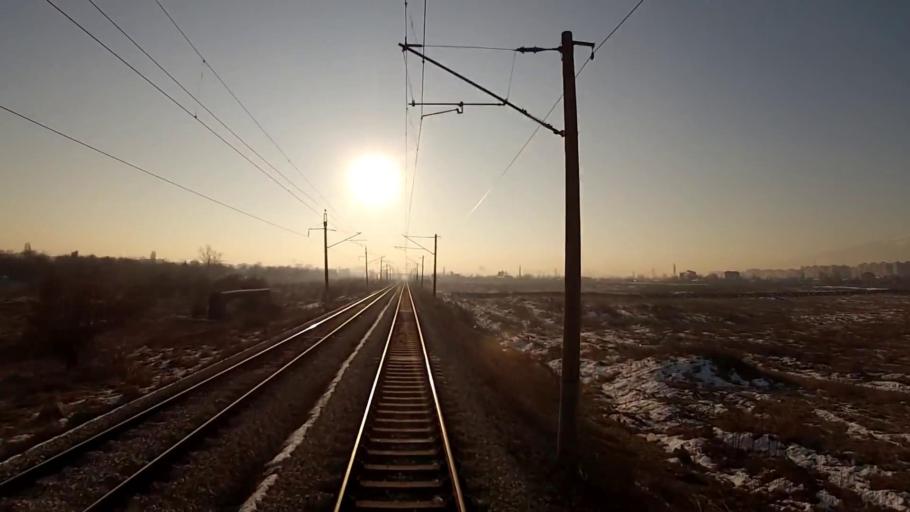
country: BG
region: Sofiya
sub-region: Obshtina Bozhurishte
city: Bozhurishte
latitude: 42.7415
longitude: 23.2605
